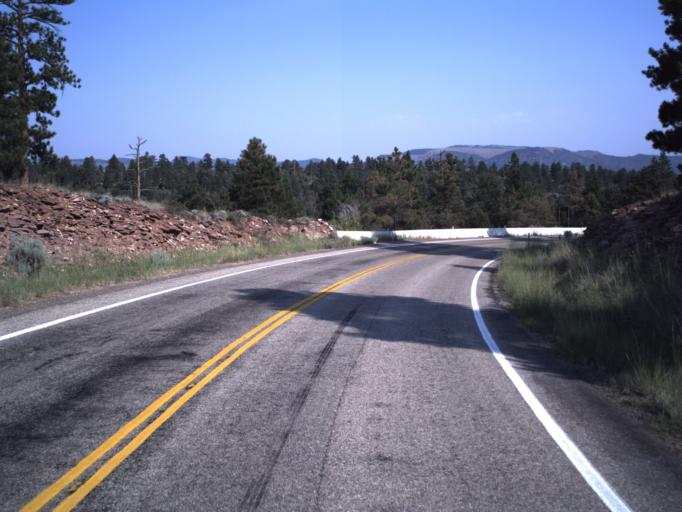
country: US
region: Utah
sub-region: Daggett County
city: Manila
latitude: 40.8915
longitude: -109.4583
